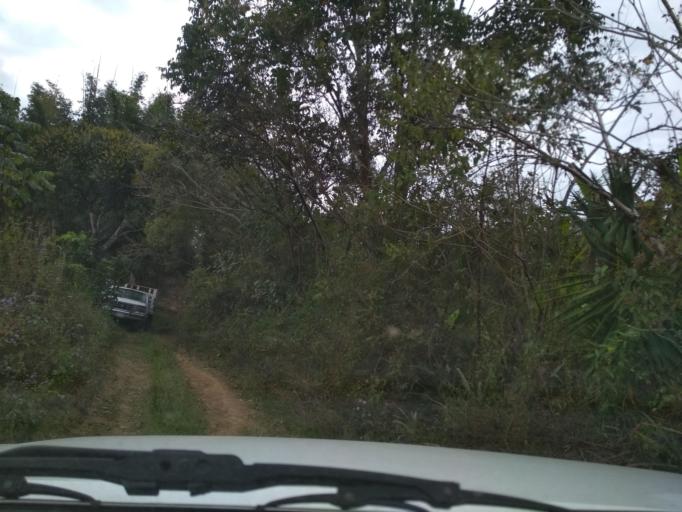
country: MX
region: Veracruz
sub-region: Coatepec
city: Tuzamapan
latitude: 19.3669
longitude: -96.8840
